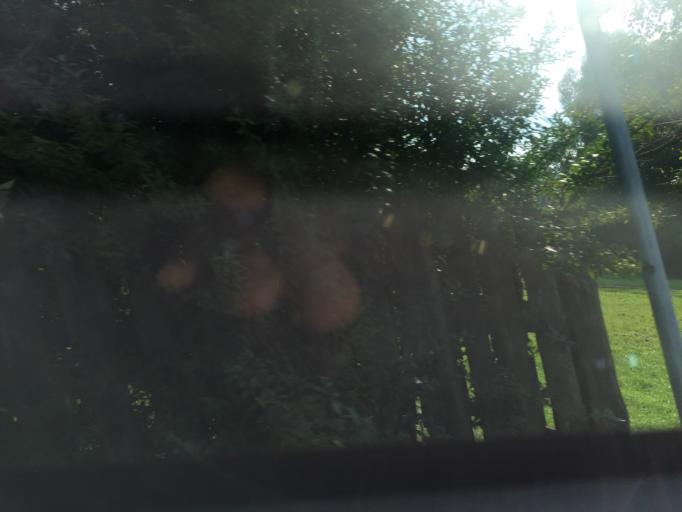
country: CZ
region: Ustecky
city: Ceska Kamenice
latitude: 50.8212
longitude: 14.3540
